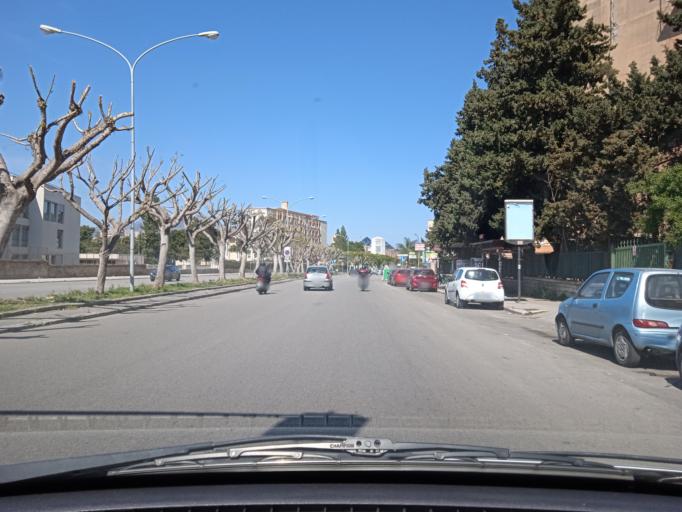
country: IT
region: Sicily
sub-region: Palermo
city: Palermo
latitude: 38.1007
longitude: 13.3476
